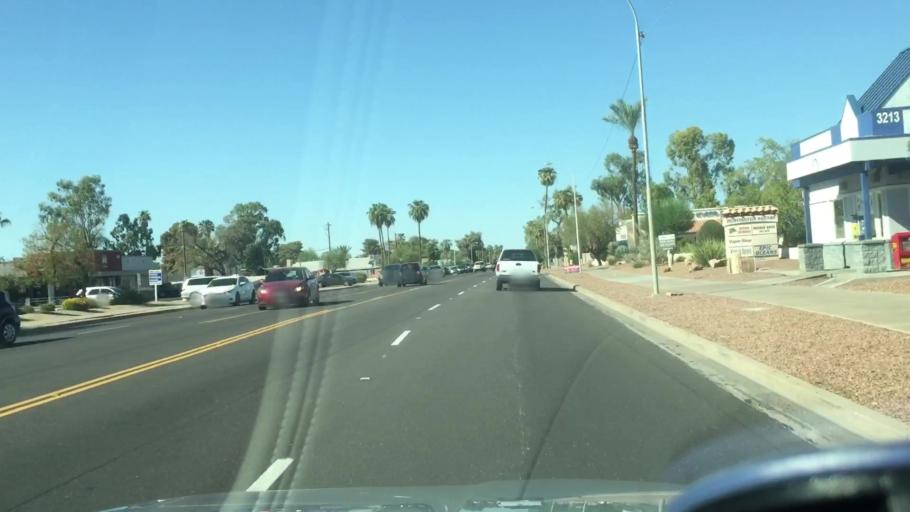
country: US
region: Arizona
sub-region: Maricopa County
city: Tempe Junction
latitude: 33.3938
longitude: -111.9395
